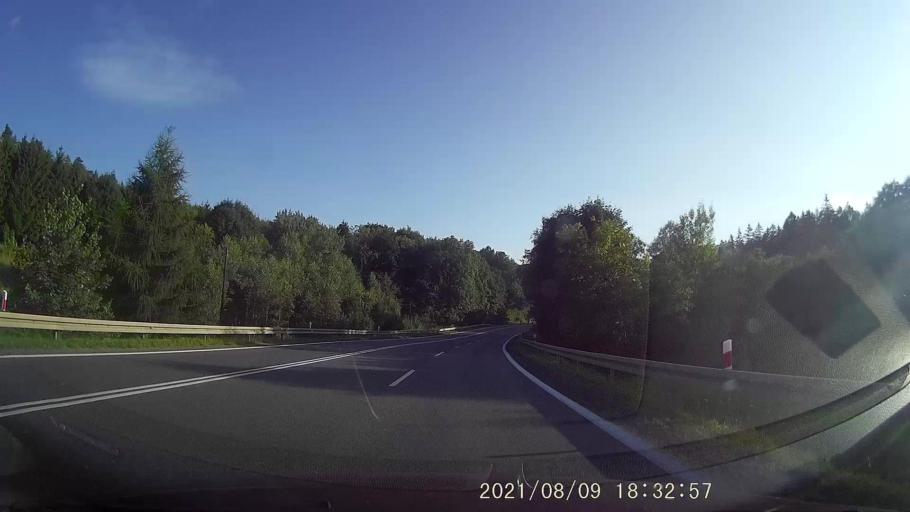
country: PL
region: Lower Silesian Voivodeship
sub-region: Powiat zabkowicki
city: Bardo
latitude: 50.4937
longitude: 16.7248
